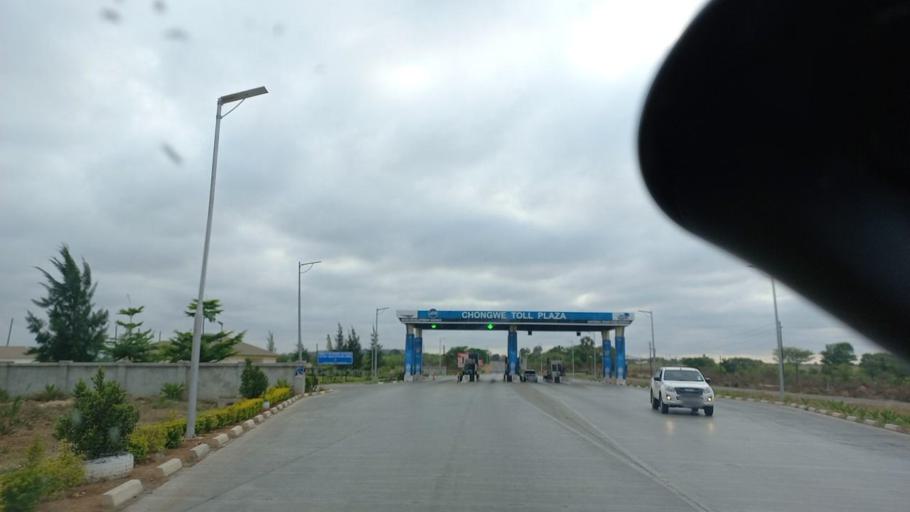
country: ZM
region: Lusaka
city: Chongwe
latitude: -15.3480
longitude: 28.5748
